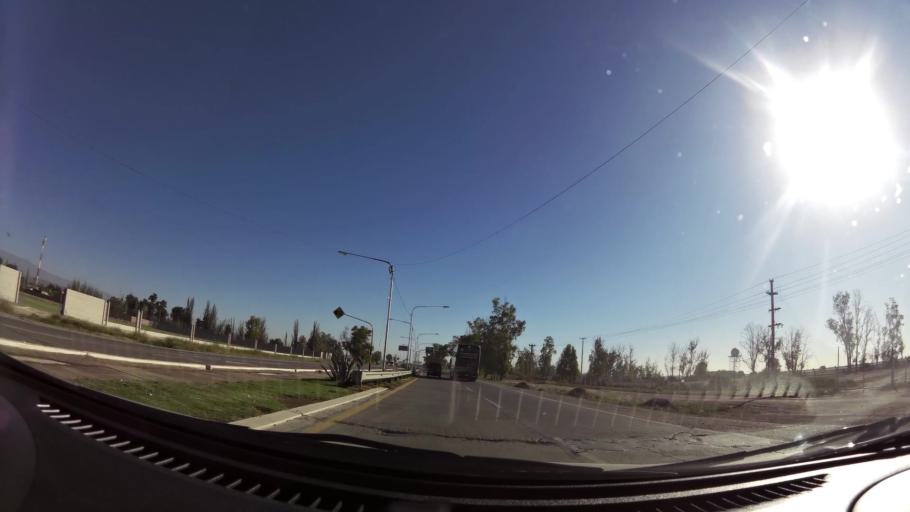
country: AR
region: Mendoza
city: Las Heras
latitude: -32.8266
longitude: -68.8041
